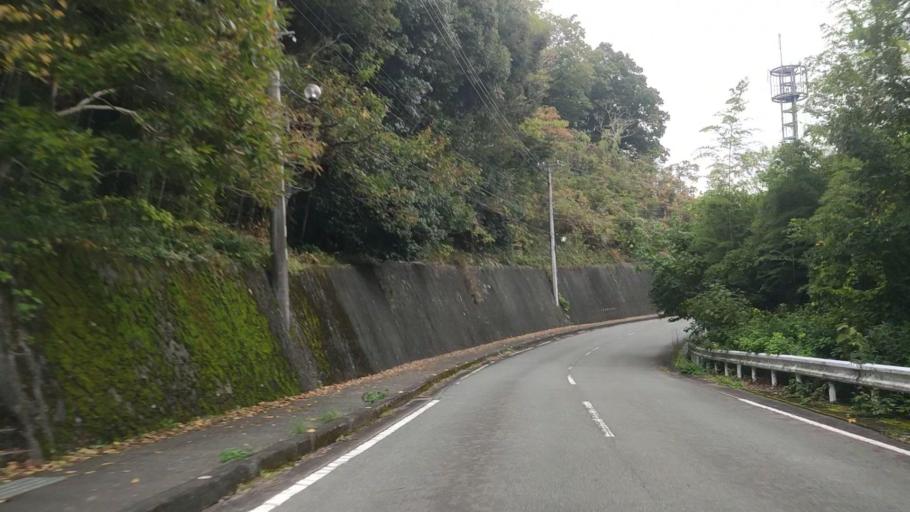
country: JP
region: Shizuoka
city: Heda
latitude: 34.9205
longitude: 138.9239
